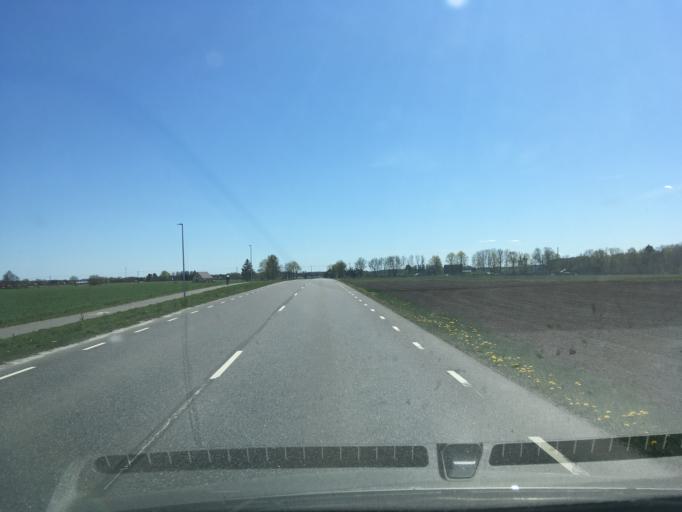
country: EE
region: Harju
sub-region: Maardu linn
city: Maardu
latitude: 59.4428
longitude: 25.0702
